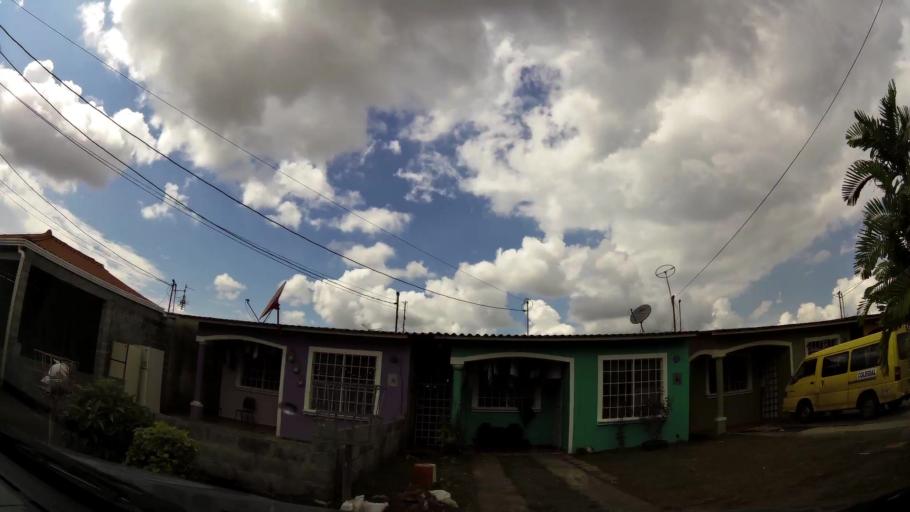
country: PA
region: Panama
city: Nuevo Arraijan
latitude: 8.9351
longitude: -79.7257
